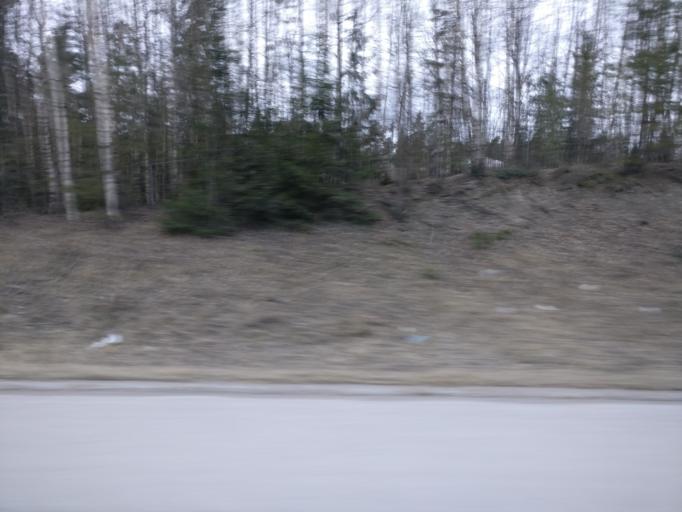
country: FI
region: Uusimaa
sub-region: Helsinki
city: Nurmijaervi
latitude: 60.4114
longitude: 24.8239
